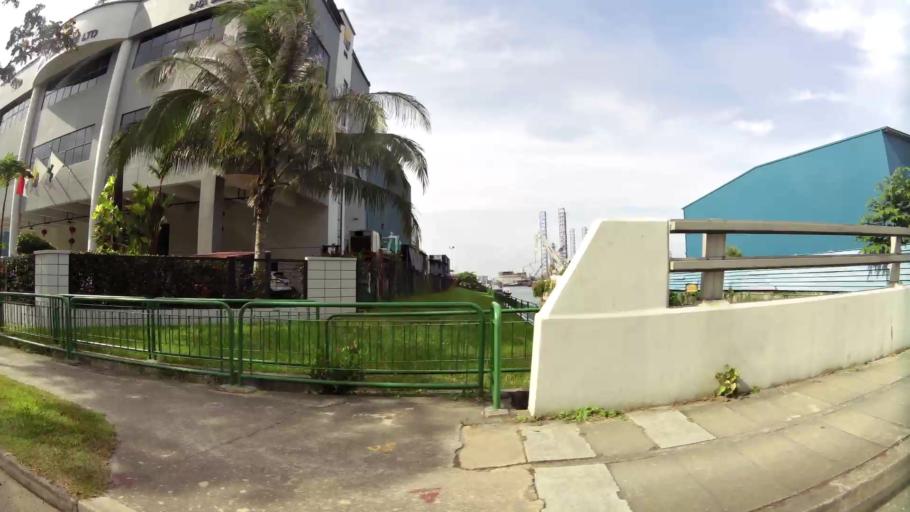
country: MY
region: Johor
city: Johor Bahru
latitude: 1.3171
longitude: 103.6515
